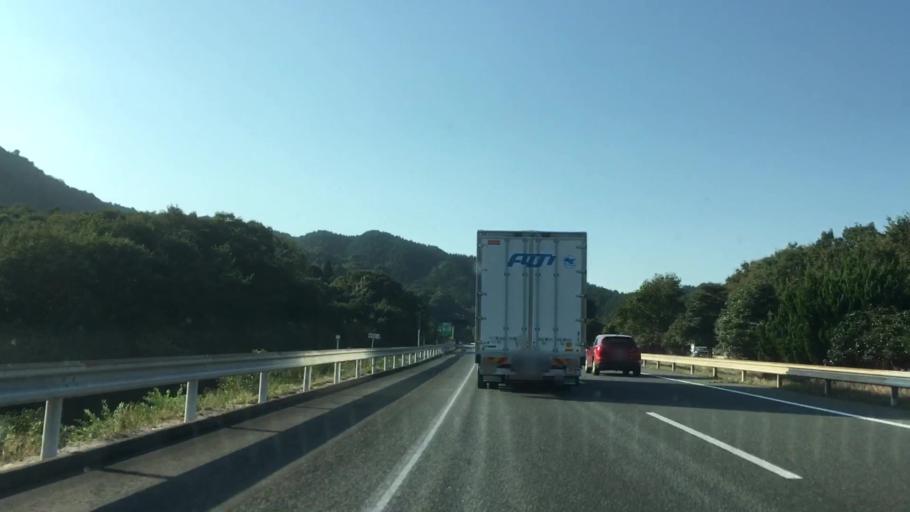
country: JP
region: Yamaguchi
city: Hofu
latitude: 34.0760
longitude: 131.4916
